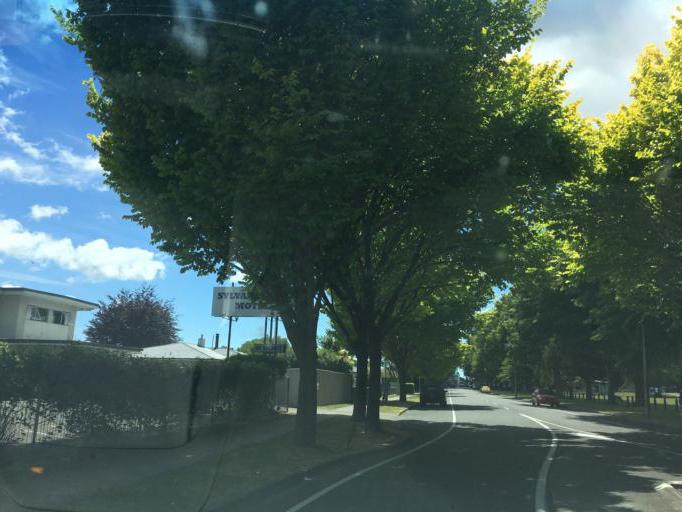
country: NZ
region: Hawke's Bay
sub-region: Hastings District
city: Hastings
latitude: -39.6437
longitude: 176.8606
